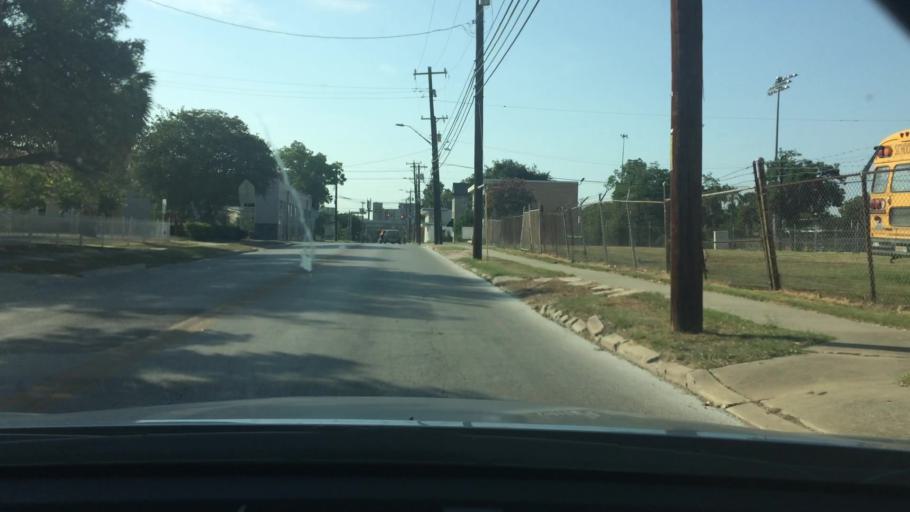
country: US
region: Texas
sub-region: Bexar County
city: San Antonio
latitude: 29.4354
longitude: -98.4872
